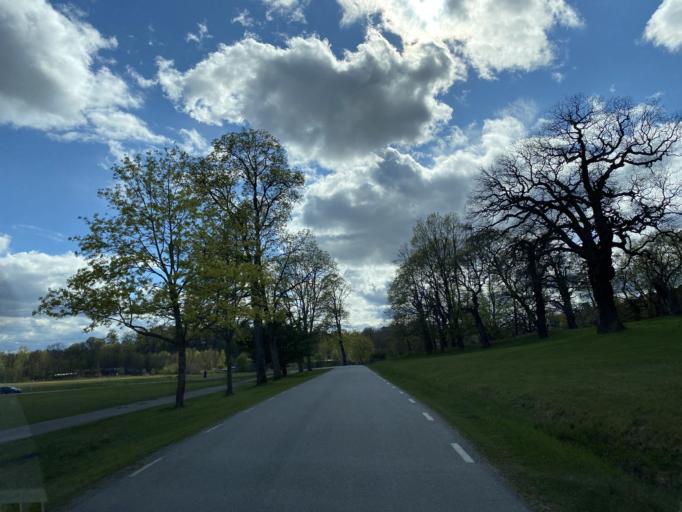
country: SE
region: Stockholm
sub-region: Stockholms Kommun
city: OEstermalm
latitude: 59.3647
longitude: 18.0864
